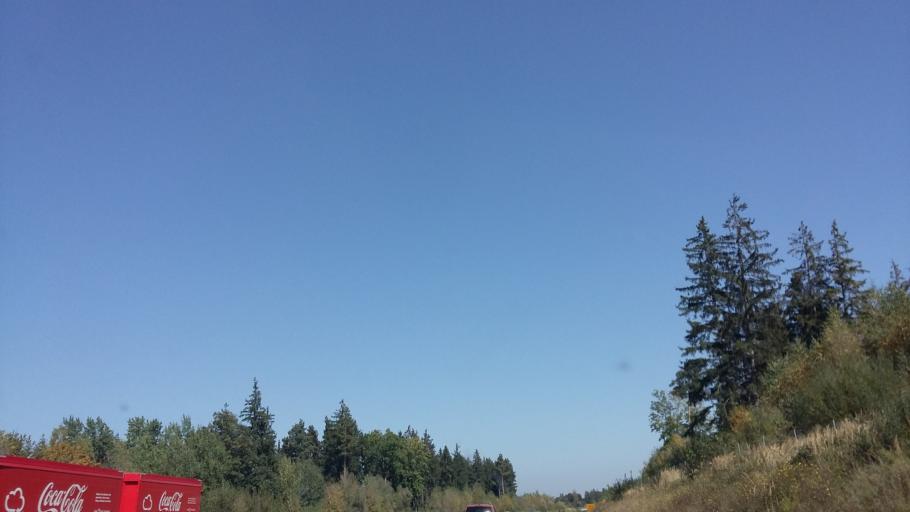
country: DE
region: Bavaria
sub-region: Upper Bavaria
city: Hurlach
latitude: 48.0667
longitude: 10.8291
